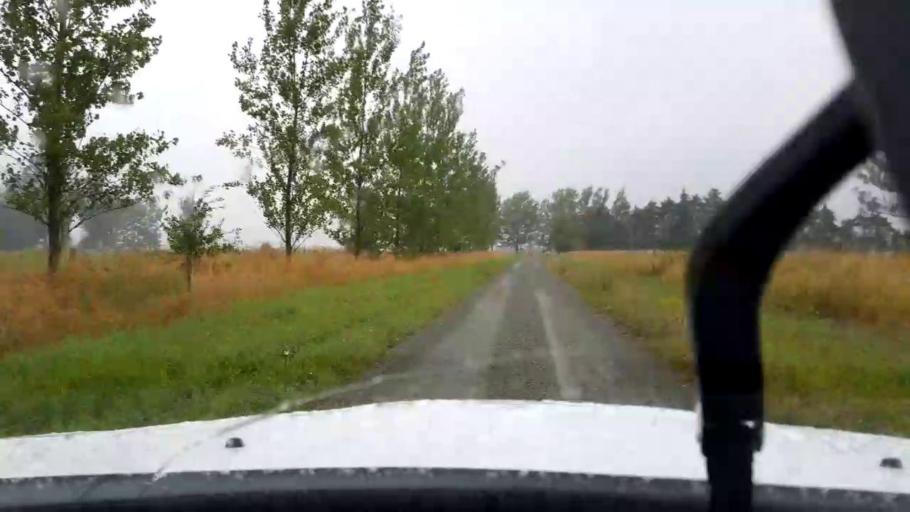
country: NZ
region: Canterbury
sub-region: Timaru District
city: Pleasant Point
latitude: -44.2017
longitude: 171.0899
